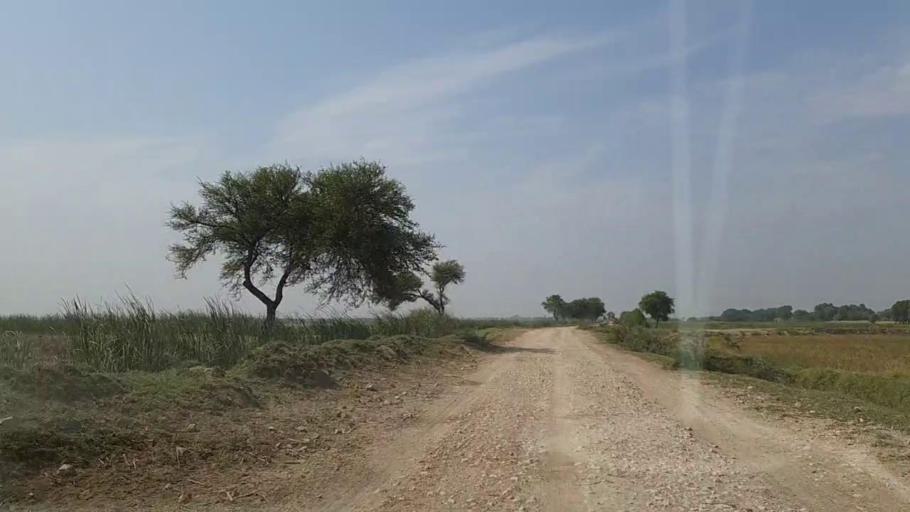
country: PK
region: Sindh
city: Mirpur Batoro
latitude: 24.6111
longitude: 68.2275
